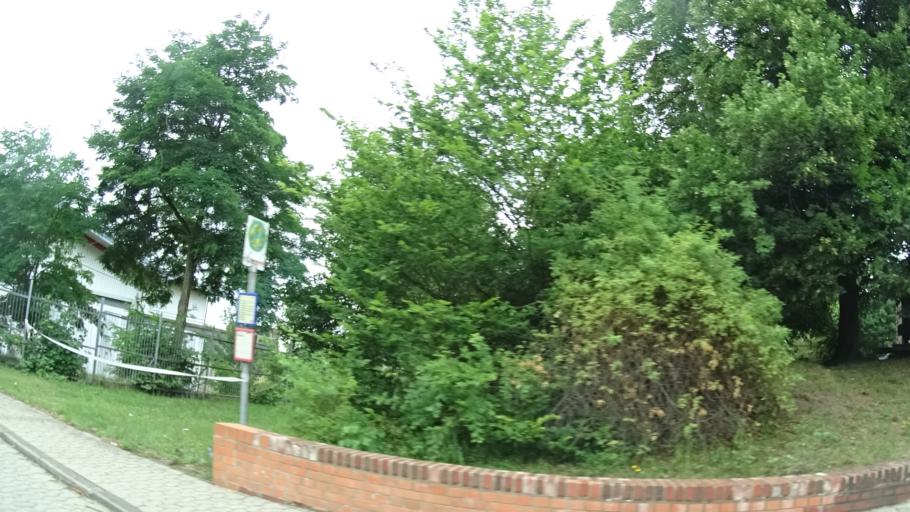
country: DE
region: Saarland
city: Merchweiler
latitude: 49.3444
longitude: 7.0391
